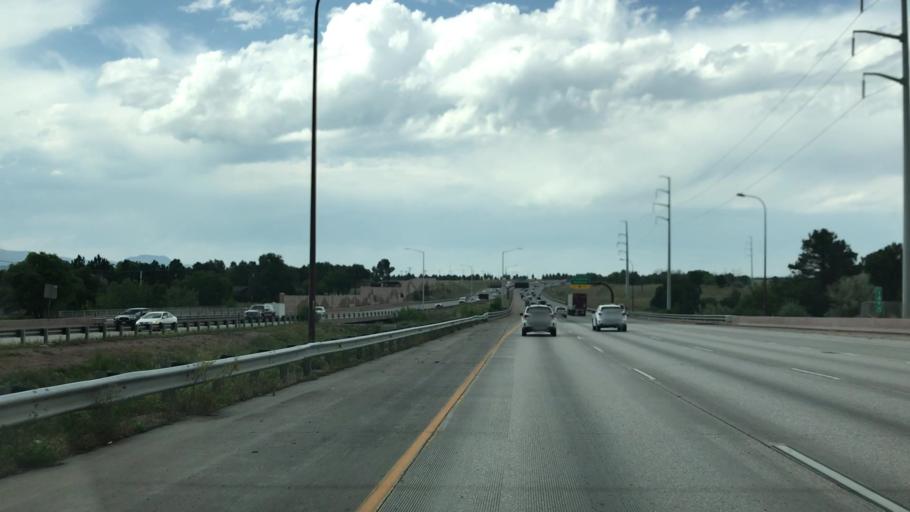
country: US
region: Colorado
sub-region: El Paso County
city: Air Force Academy
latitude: 38.9377
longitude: -104.8126
